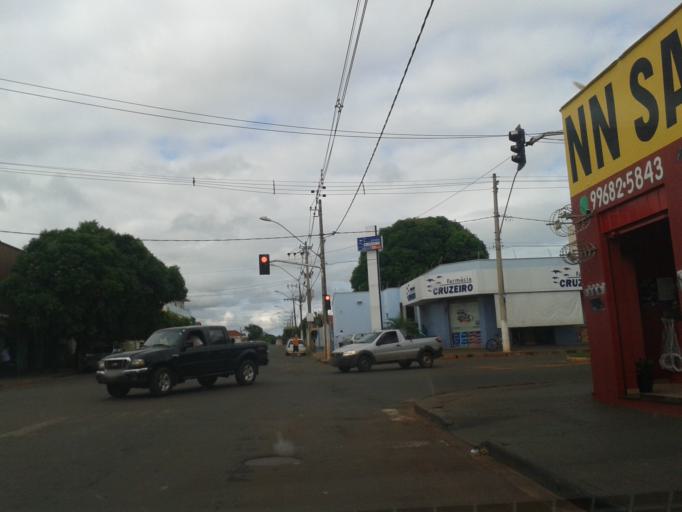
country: BR
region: Minas Gerais
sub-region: Ituiutaba
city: Ituiutaba
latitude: -18.9801
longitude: -49.4794
